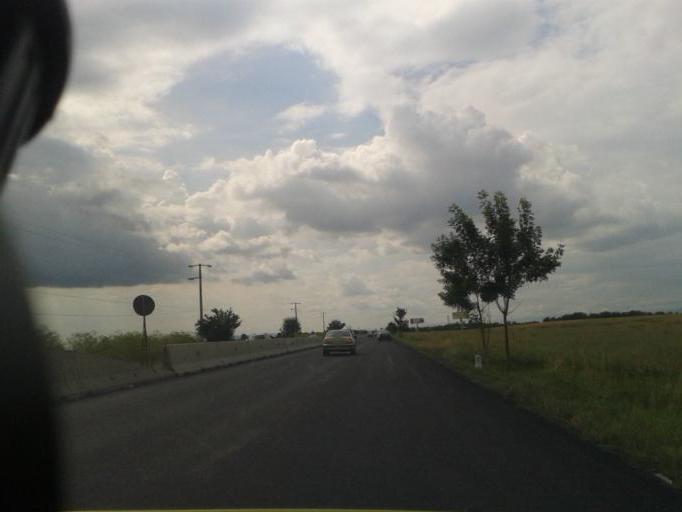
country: RO
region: Prahova
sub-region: Comuna Paulesti
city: Gageni
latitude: 44.9809
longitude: 25.9340
